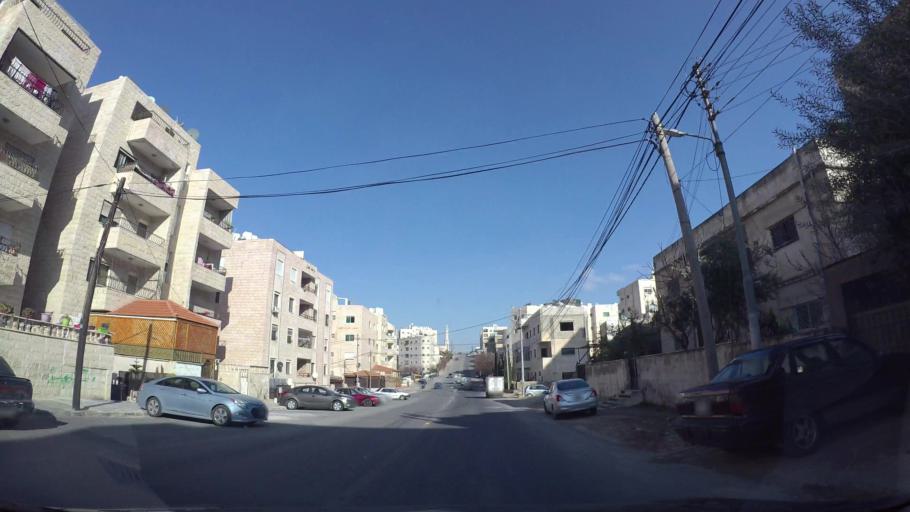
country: JO
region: Amman
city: Amman
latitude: 31.9802
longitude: 35.9527
